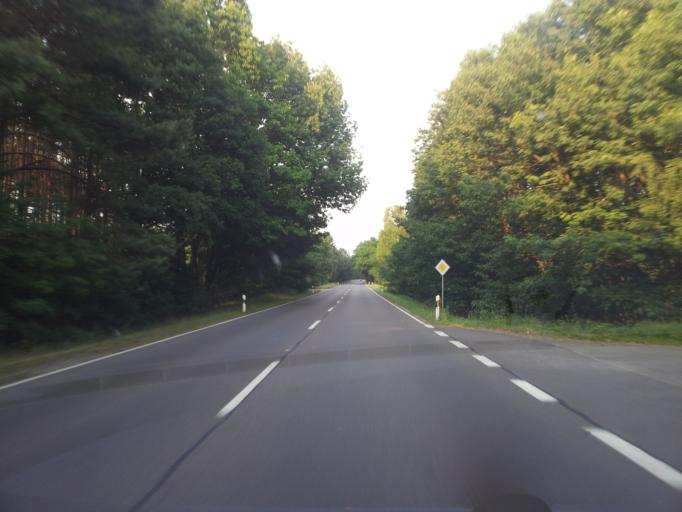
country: DE
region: Saxony
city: Ossling
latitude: 51.4142
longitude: 14.1628
